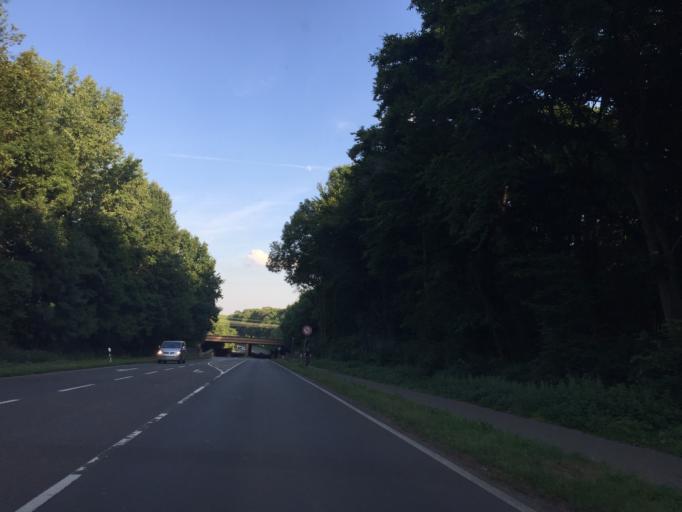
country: DE
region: North Rhine-Westphalia
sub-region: Regierungsbezirk Koln
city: Neustadt/Sued
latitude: 50.8997
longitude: 6.9211
